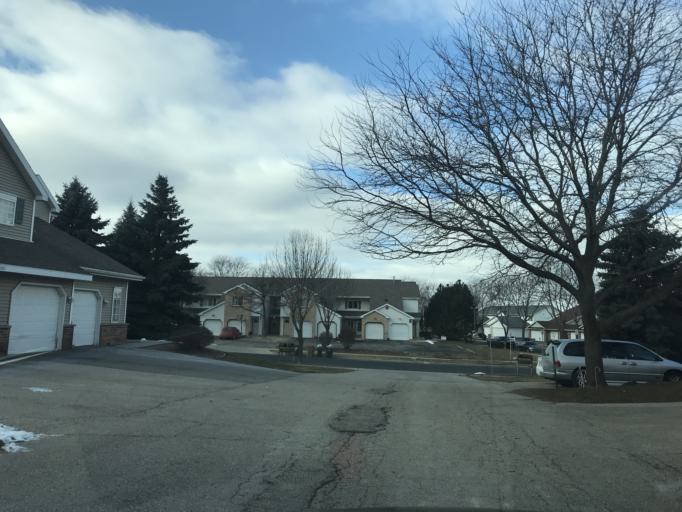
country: US
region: Wisconsin
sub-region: Dane County
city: Monona
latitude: 43.1120
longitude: -89.2972
